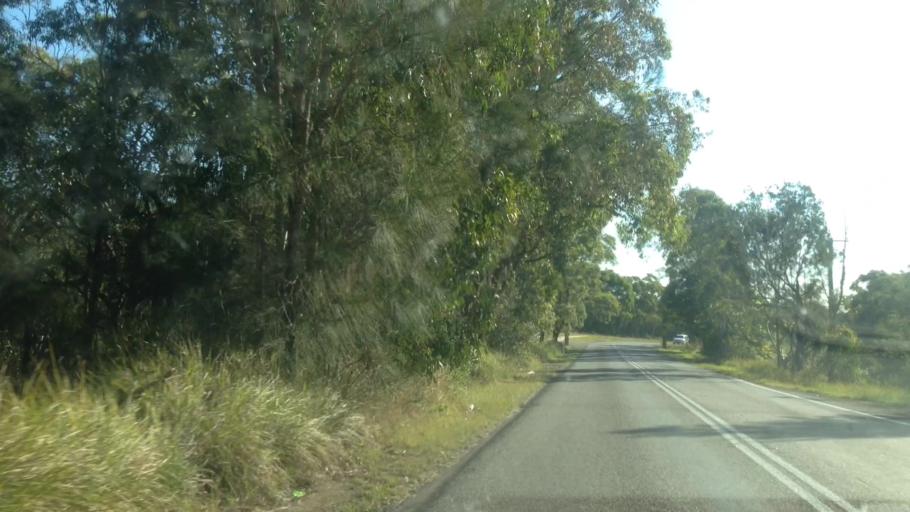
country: AU
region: New South Wales
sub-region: Lake Macquarie Shire
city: Dora Creek
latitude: -33.1080
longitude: 151.5403
